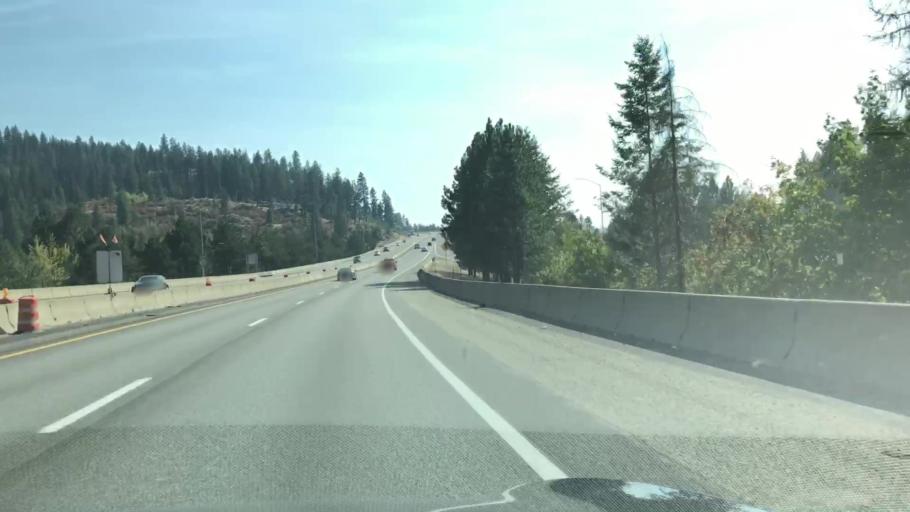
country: US
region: Idaho
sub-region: Kootenai County
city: Coeur d'Alene
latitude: 47.6727
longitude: -116.7512
